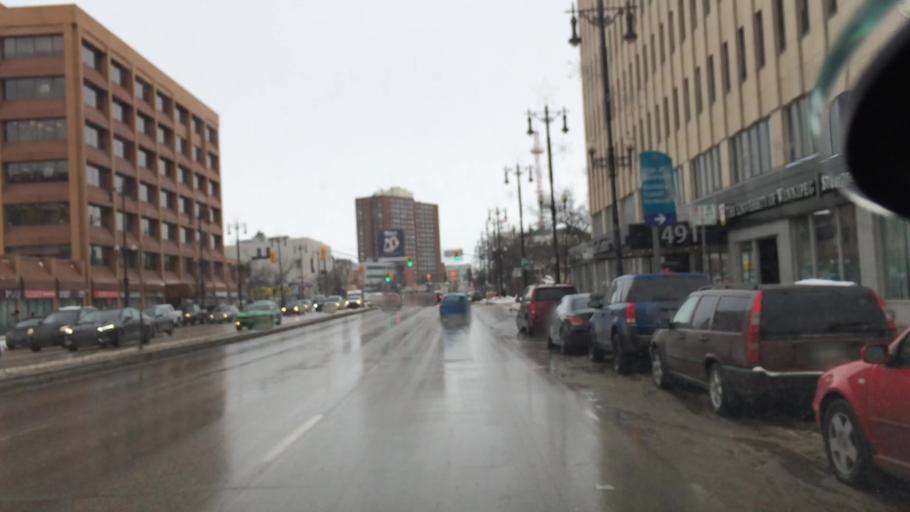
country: CA
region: Manitoba
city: Winnipeg
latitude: 49.8909
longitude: -97.1515
